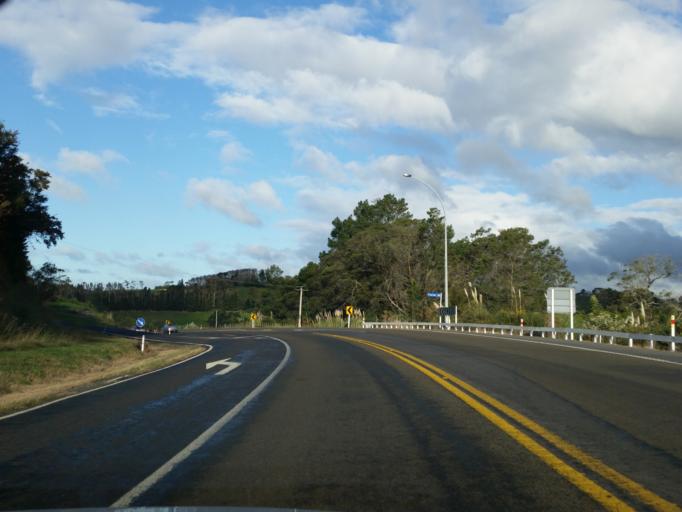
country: NZ
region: Bay of Plenty
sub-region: Western Bay of Plenty District
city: Katikati
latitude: -37.6494
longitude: 175.9682
